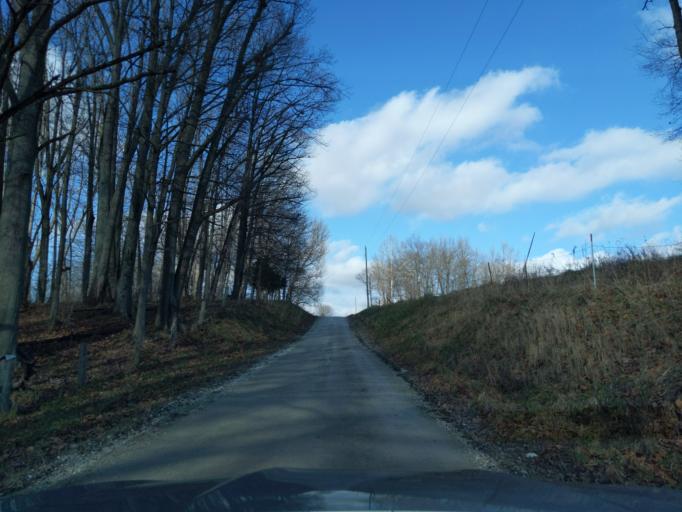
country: US
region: Indiana
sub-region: Decatur County
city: Greensburg
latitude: 39.2585
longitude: -85.4842
